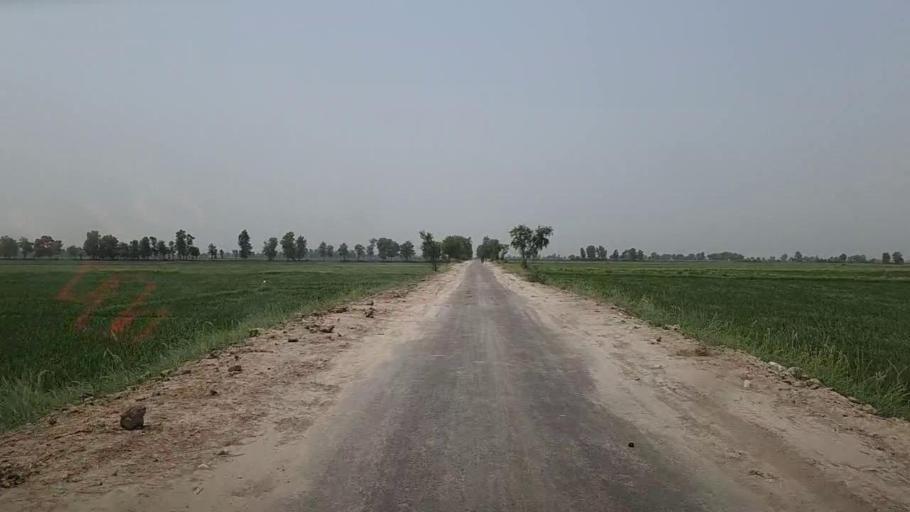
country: PK
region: Sindh
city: Sita Road
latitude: 27.0765
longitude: 67.9084
